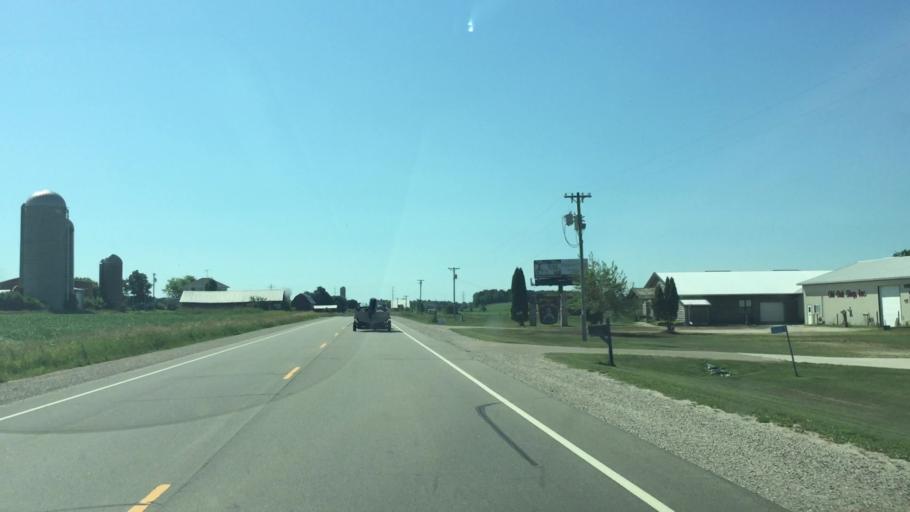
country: US
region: Wisconsin
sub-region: Calumet County
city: Chilton
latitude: 44.0072
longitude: -88.1401
